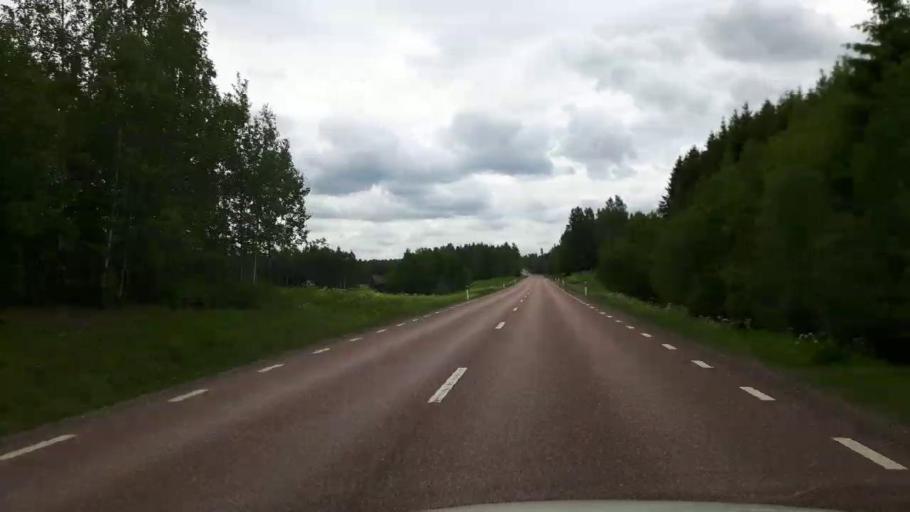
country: SE
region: Dalarna
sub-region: Hedemora Kommun
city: Brunna
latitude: 60.2049
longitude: 15.9929
